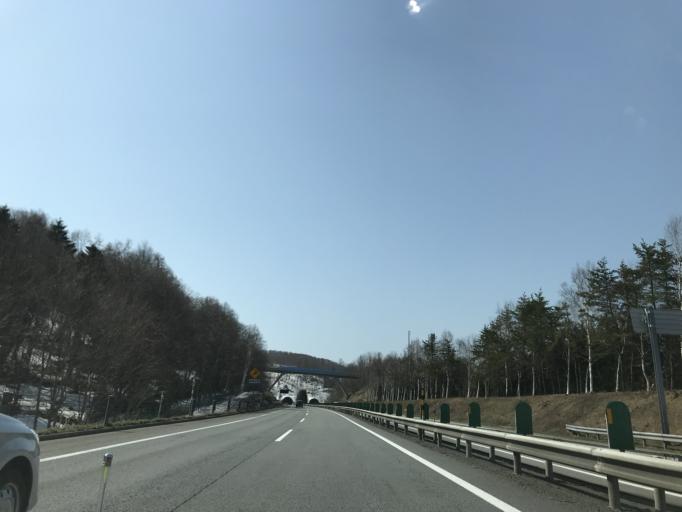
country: JP
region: Hokkaido
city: Bibai
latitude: 43.3136
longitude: 141.8825
